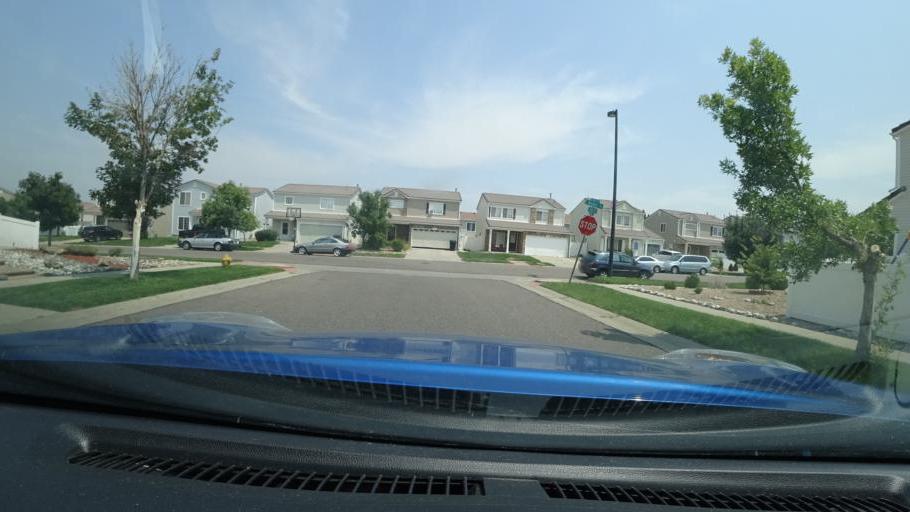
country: US
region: Colorado
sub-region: Adams County
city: Aurora
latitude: 39.7726
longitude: -104.7691
